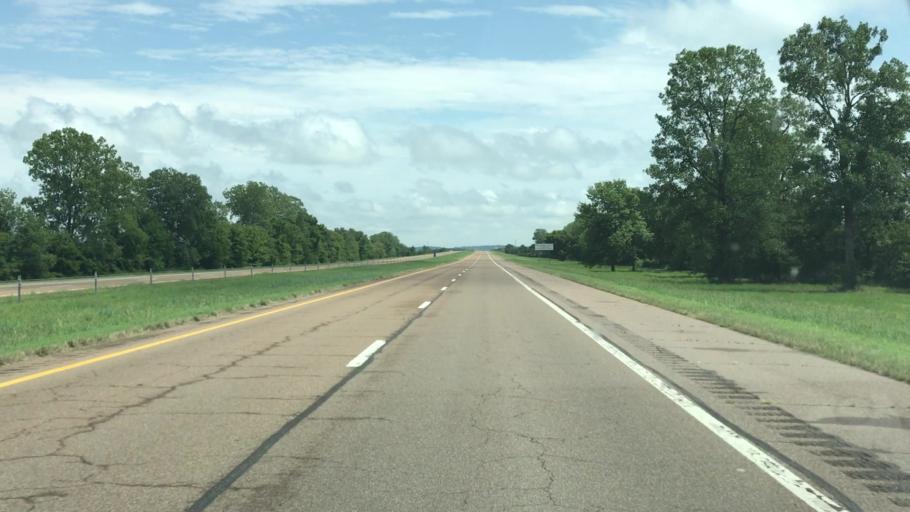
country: US
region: Missouri
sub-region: Pemiscot County
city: Caruthersville
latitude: 36.0911
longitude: -89.5769
